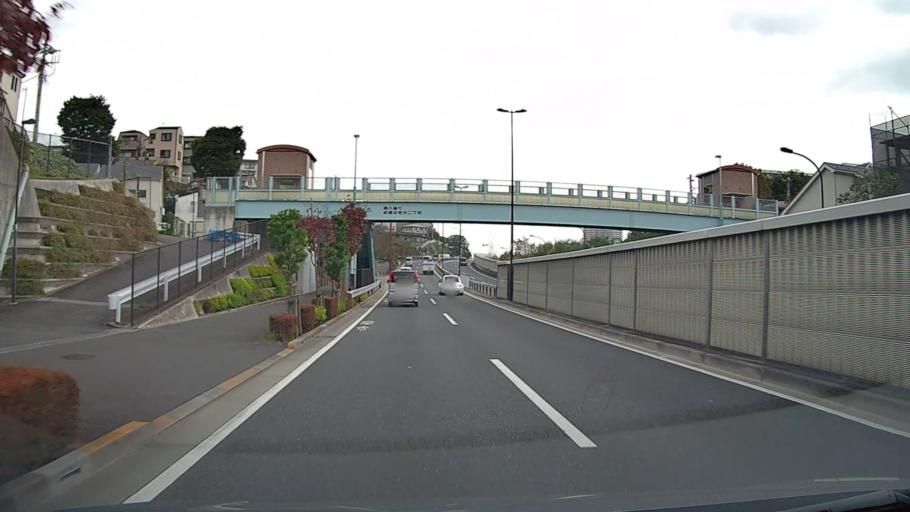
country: JP
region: Saitama
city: Shimotoda
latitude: 35.7705
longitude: 139.6706
